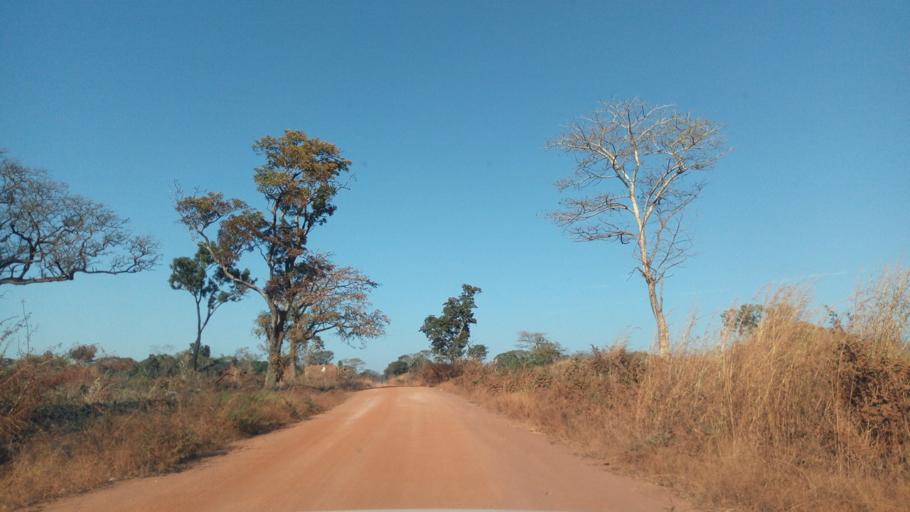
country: ZM
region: Luapula
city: Mwense
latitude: -10.5445
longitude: 28.4486
